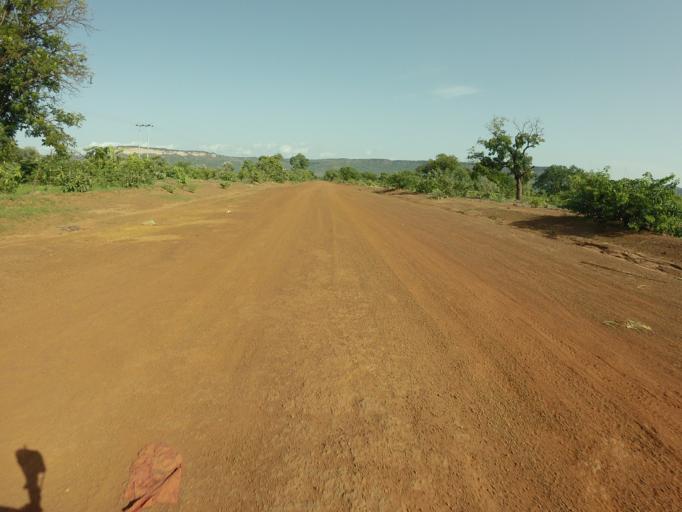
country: GH
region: Upper East
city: Bawku
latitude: 10.6824
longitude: -0.2144
